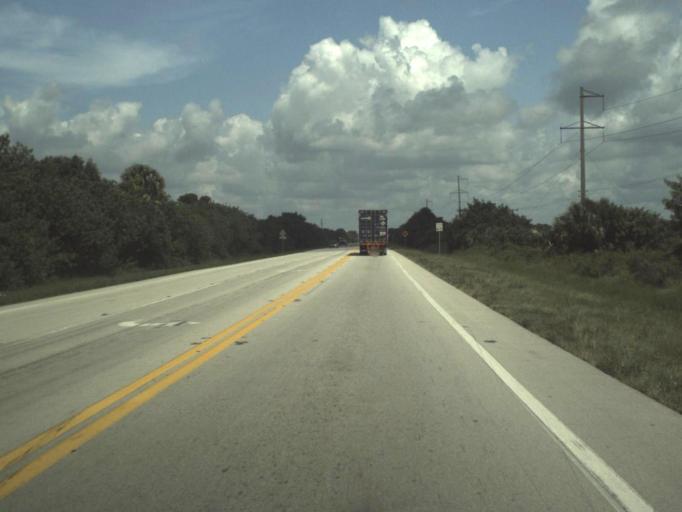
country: US
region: Florida
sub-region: Okeechobee County
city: Taylor Creek
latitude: 27.1593
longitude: -80.6777
